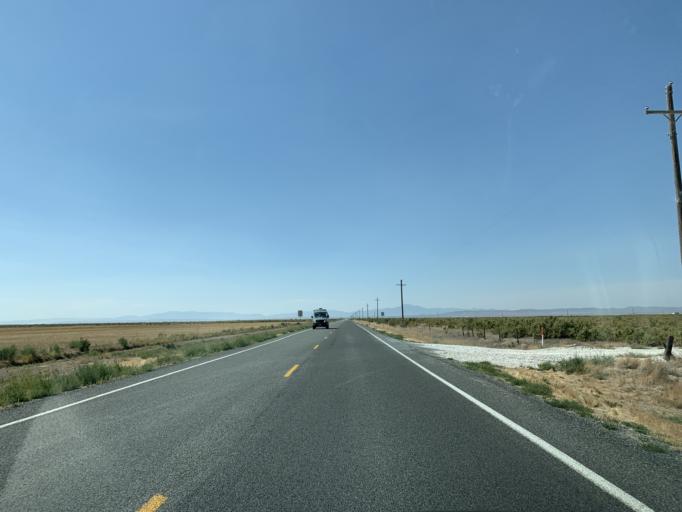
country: US
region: Utah
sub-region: Millard County
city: Delta
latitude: 39.3309
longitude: -112.6849
